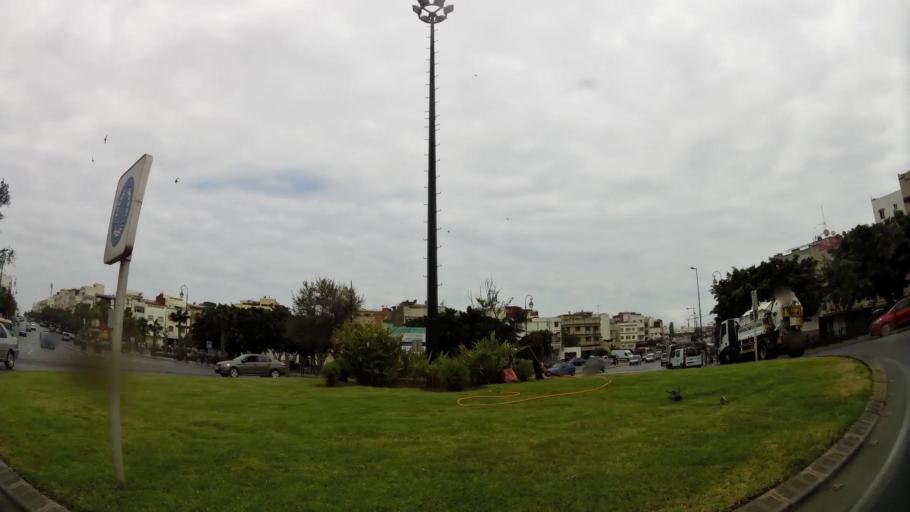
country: MA
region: Rabat-Sale-Zemmour-Zaer
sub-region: Rabat
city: Rabat
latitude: 33.9909
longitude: -6.8713
